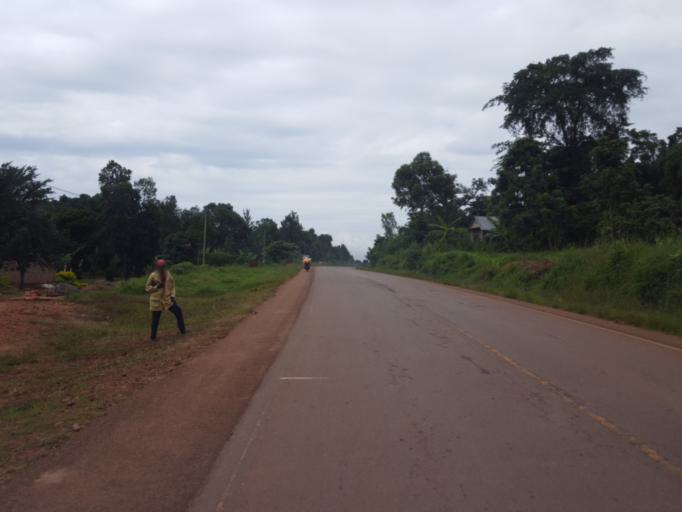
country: UG
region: Central Region
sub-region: Mityana District
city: Mityana
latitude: 0.6507
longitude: 32.0952
